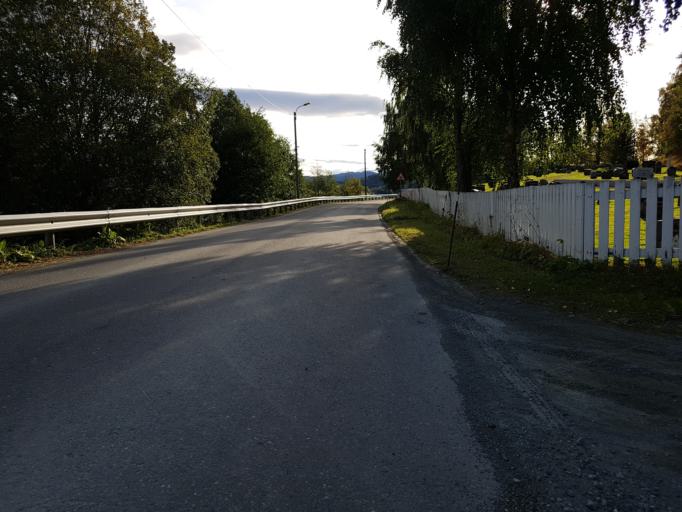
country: NO
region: Sor-Trondelag
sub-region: Klaebu
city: Klaebu
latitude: 63.3480
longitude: 10.4832
